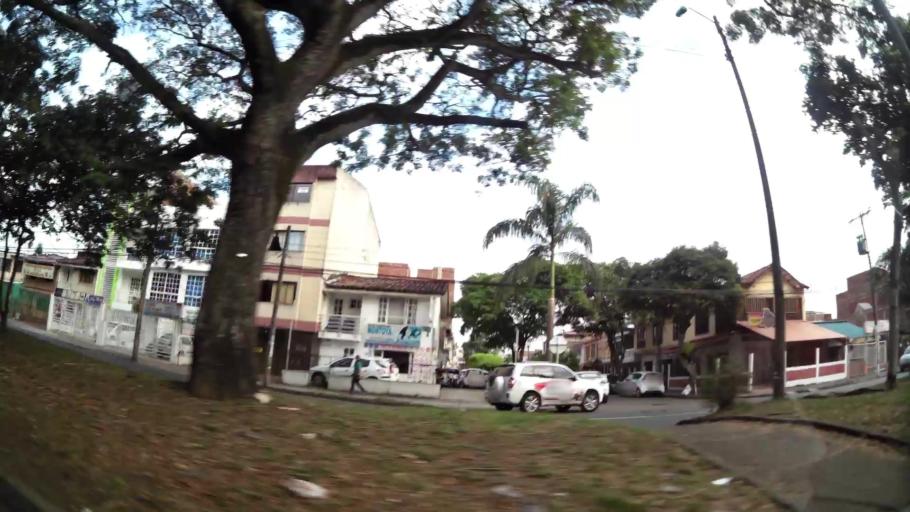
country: CO
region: Valle del Cauca
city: Cali
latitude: 3.4690
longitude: -76.4992
